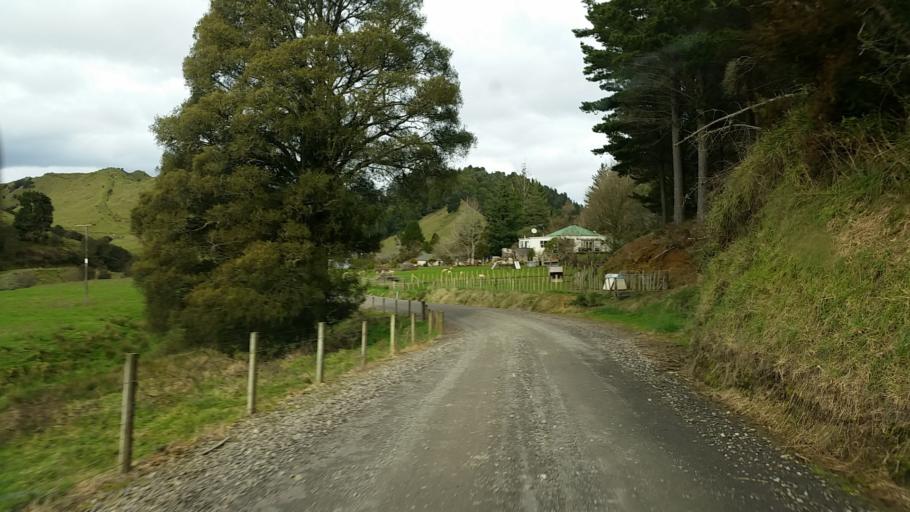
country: NZ
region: Taranaki
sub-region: New Plymouth District
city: Waitara
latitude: -39.1572
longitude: 174.5613
